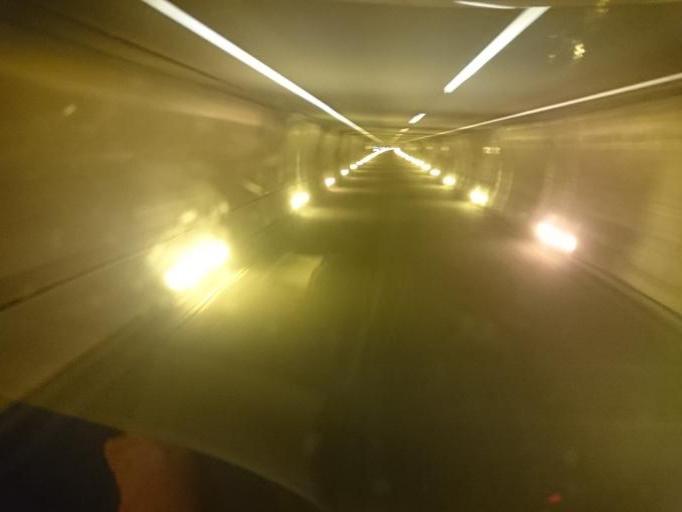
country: ES
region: Castille and Leon
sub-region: Provincia de Leon
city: Sena de Luna
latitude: 42.9778
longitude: -5.8318
